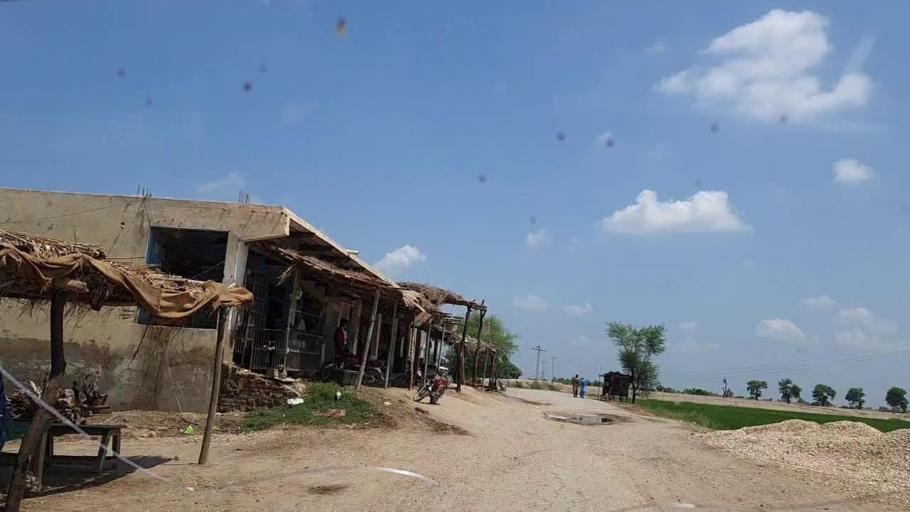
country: PK
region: Sindh
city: Tharu Shah
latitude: 26.9871
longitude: 68.0772
